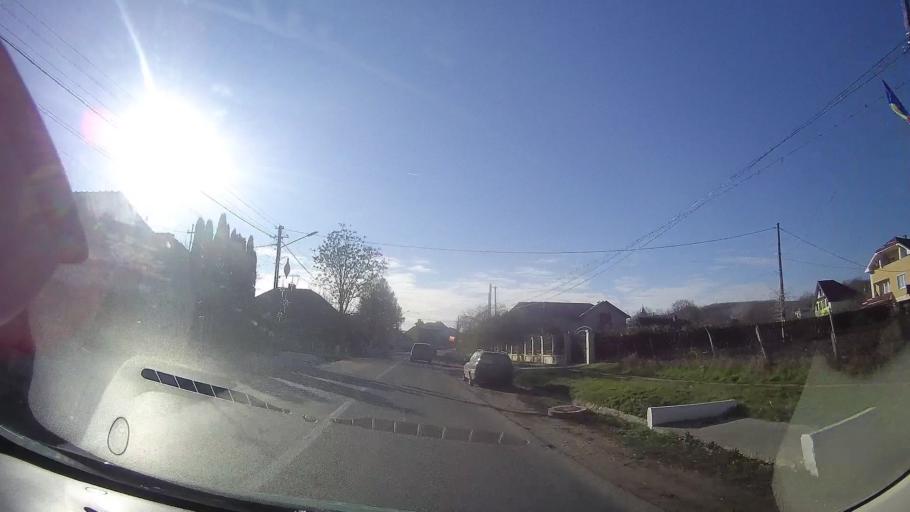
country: RO
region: Cluj
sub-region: Comuna Mociu
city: Mociu
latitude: 46.7992
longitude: 24.0366
